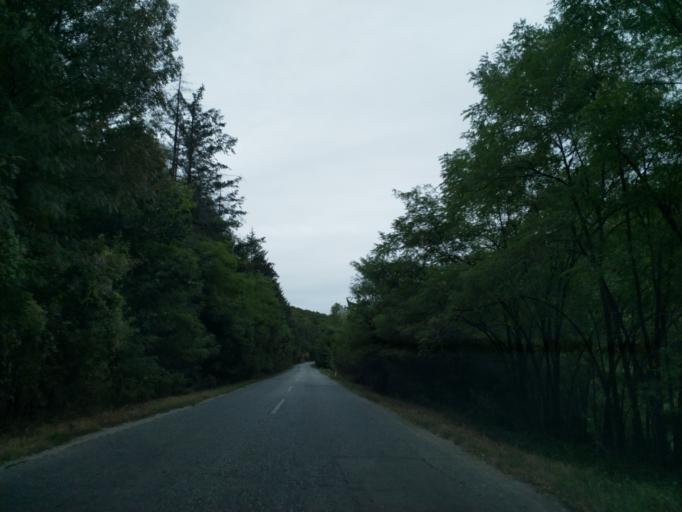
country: RS
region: Central Serbia
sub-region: Pomoravski Okrug
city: Jagodina
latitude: 44.0344
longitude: 21.1912
